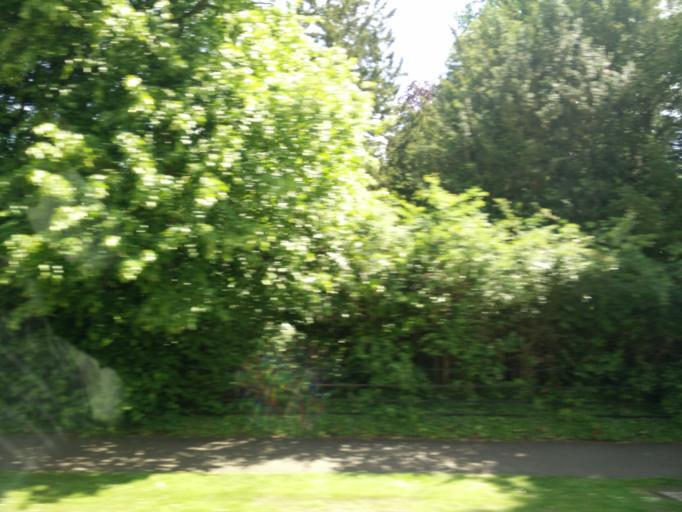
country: GB
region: England
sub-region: Cambridgeshire
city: Cambridge
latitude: 52.1875
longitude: 0.1210
